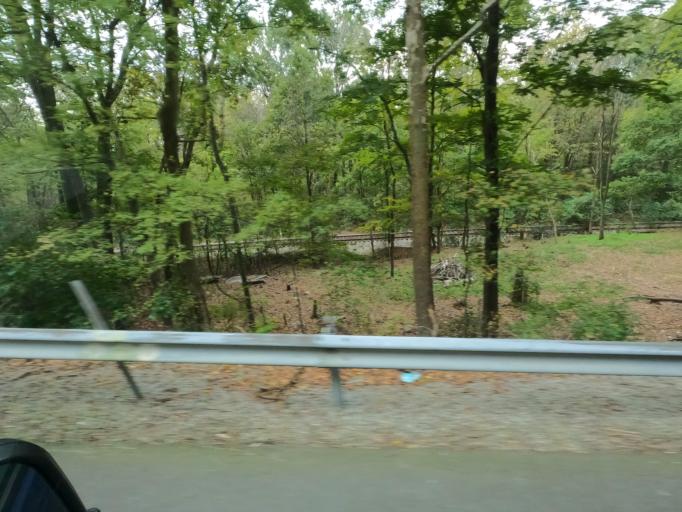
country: US
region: Tennessee
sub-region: Cheatham County
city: Pegram
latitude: 36.0942
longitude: -87.0382
